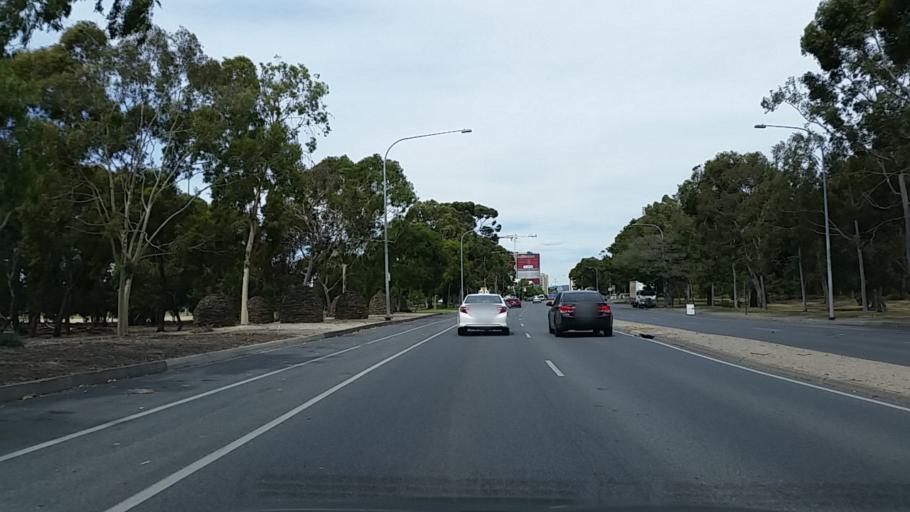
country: AU
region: South Australia
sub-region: Adelaide
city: Adelaide
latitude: -34.9295
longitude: 138.5840
